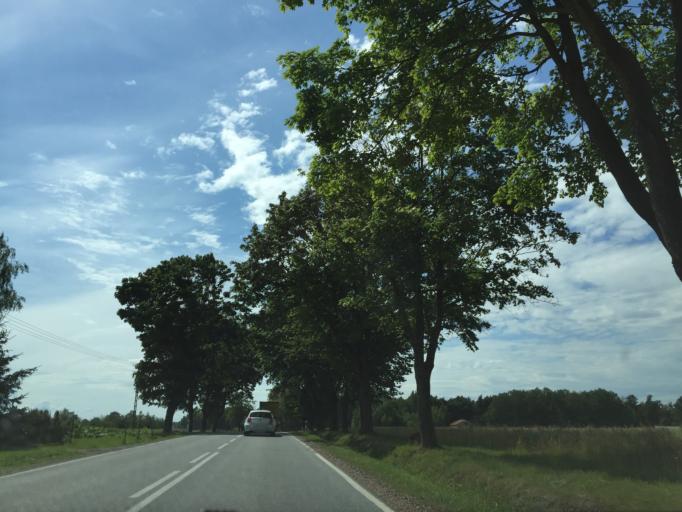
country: PL
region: Masovian Voivodeship
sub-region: Powiat losicki
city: Sarnaki
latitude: 52.3090
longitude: 22.8519
